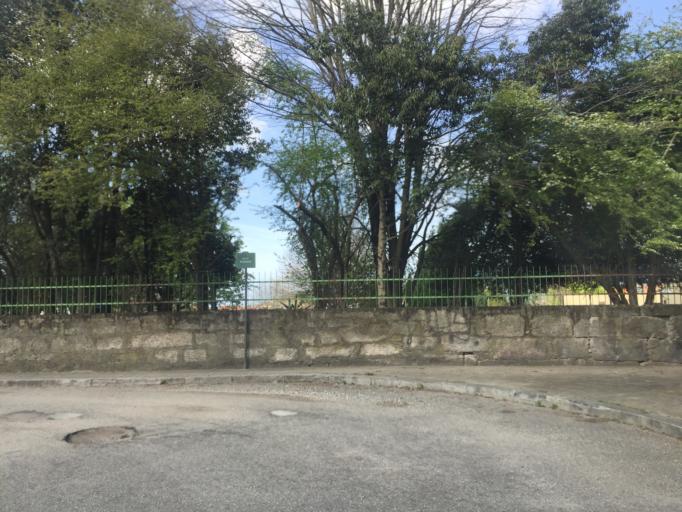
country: PT
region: Porto
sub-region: Matosinhos
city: Senhora da Hora
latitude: 41.1744
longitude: -8.6574
